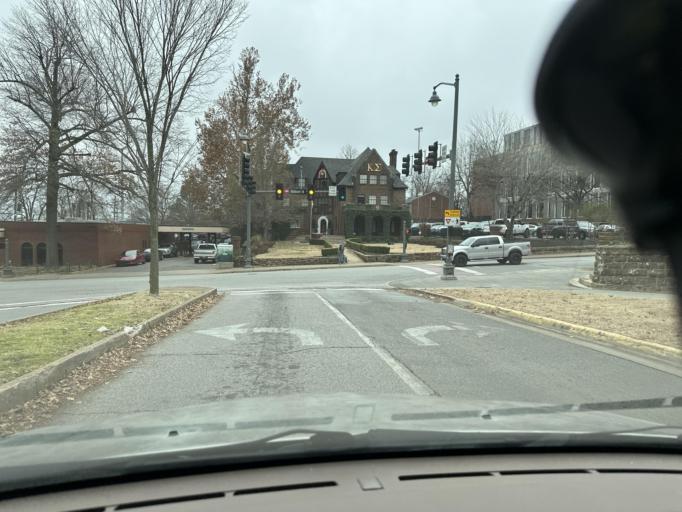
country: US
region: Arkansas
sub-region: Washington County
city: Fayetteville
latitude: 36.0668
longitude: -94.1686
